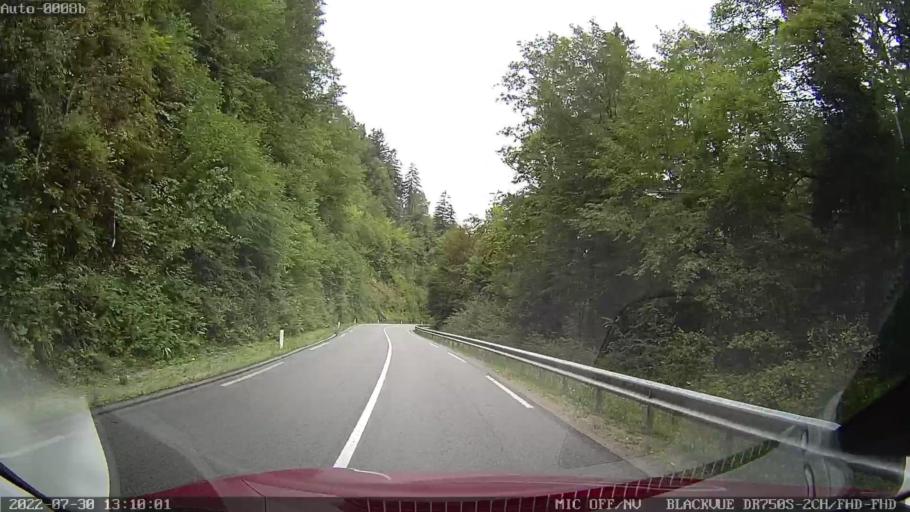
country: SI
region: Dolenjske Toplice
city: Dolenjske Toplice
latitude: 45.6913
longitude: 15.0902
